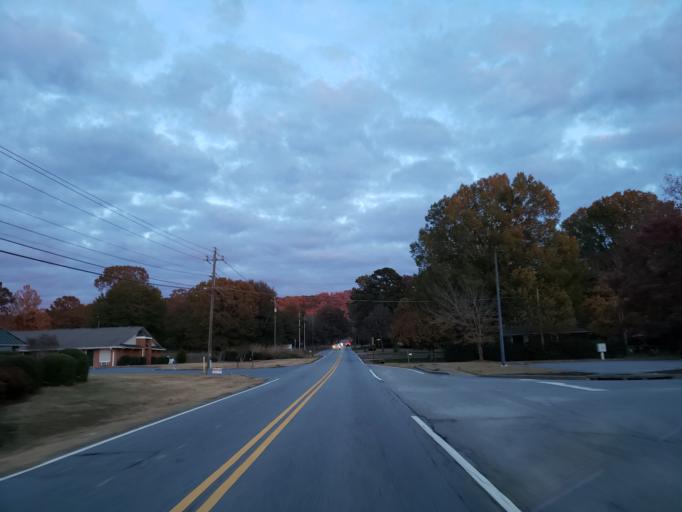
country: US
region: Georgia
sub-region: Bartow County
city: Cartersville
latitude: 34.1968
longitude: -84.7887
